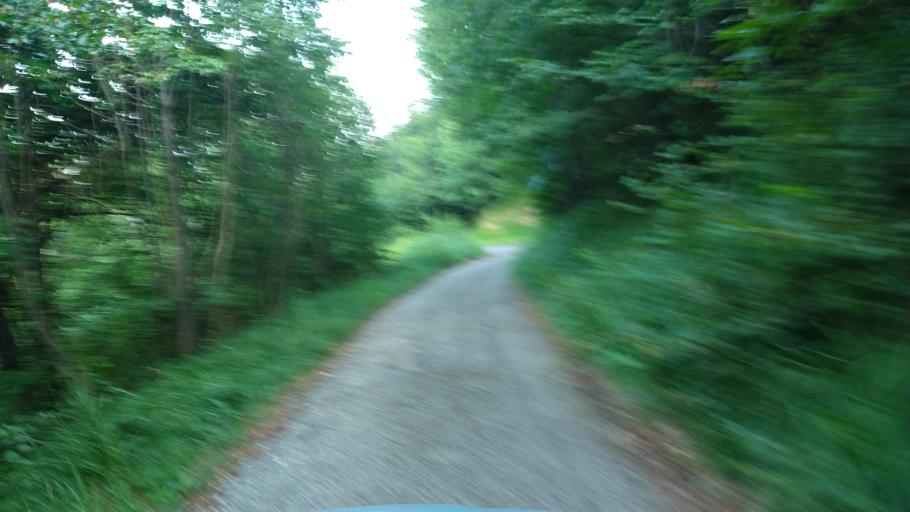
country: IT
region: Veneto
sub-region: Provincia di Vicenza
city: Campolongo sul Brenta
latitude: 45.8278
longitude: 11.6892
